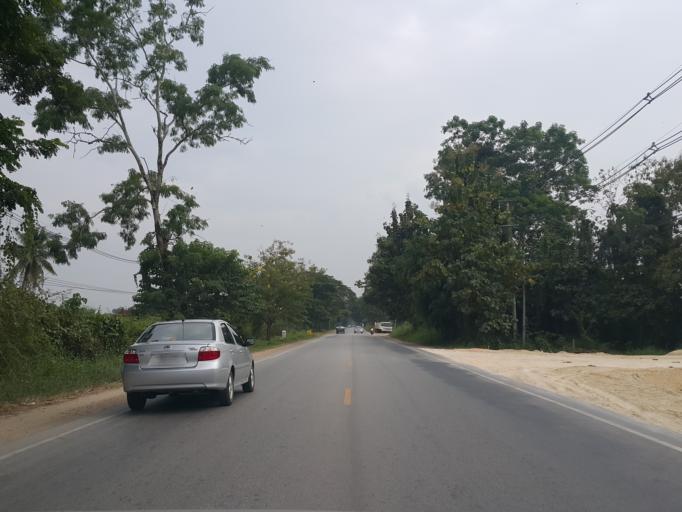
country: TH
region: Chiang Mai
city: San Sai
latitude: 18.9395
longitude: 98.9861
